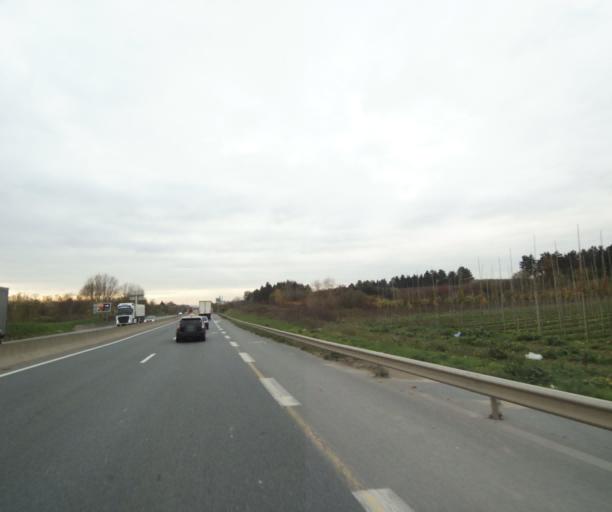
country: FR
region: Ile-de-France
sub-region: Departement du Val-d'Oise
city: Le Thillay
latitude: 48.9870
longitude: 2.4724
